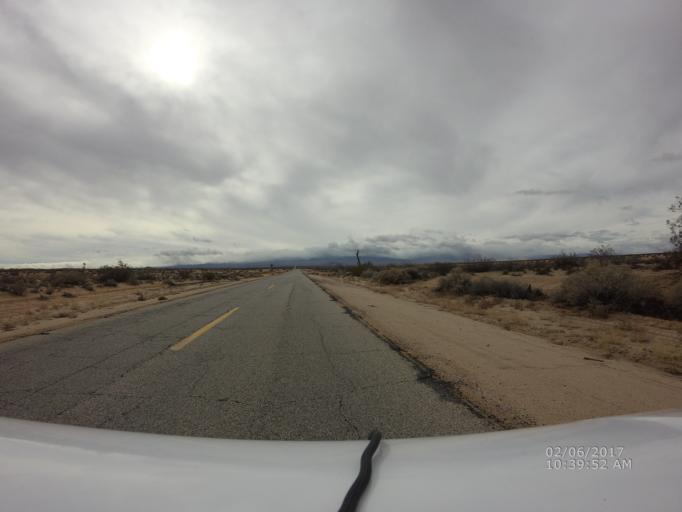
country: US
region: California
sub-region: Los Angeles County
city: Lake Los Angeles
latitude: 34.6840
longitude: -117.7024
